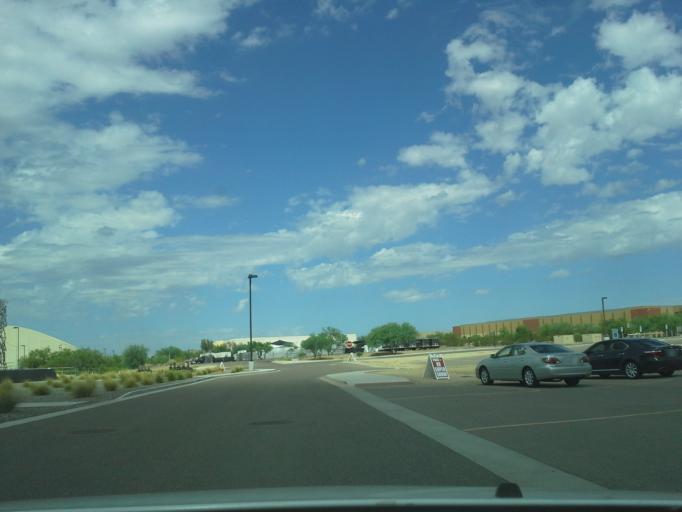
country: US
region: Arizona
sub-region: Maricopa County
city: Paradise Valley
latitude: 33.6332
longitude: -111.8774
